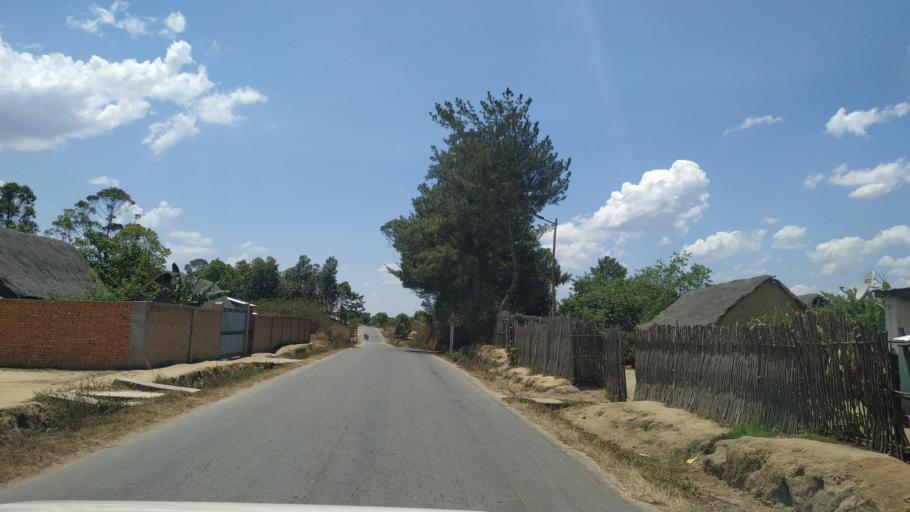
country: MG
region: Analamanga
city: Anjozorobe
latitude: -18.3014
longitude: 48.2672
